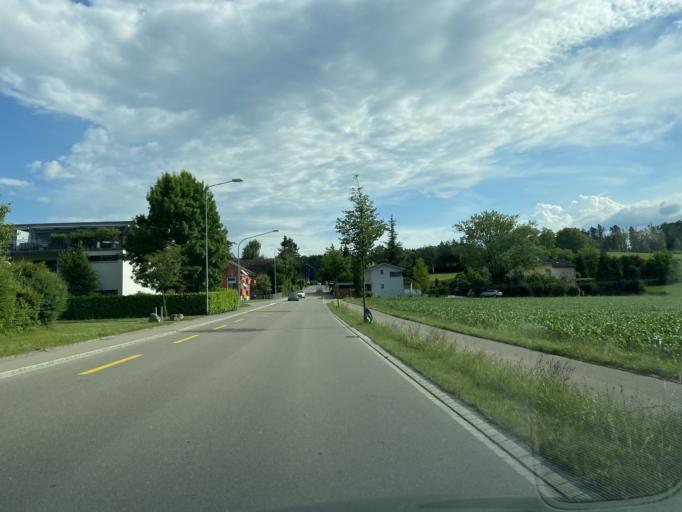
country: CH
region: Zurich
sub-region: Bezirk Winterthur
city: Seuzach Dorf
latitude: 47.5322
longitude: 8.7286
